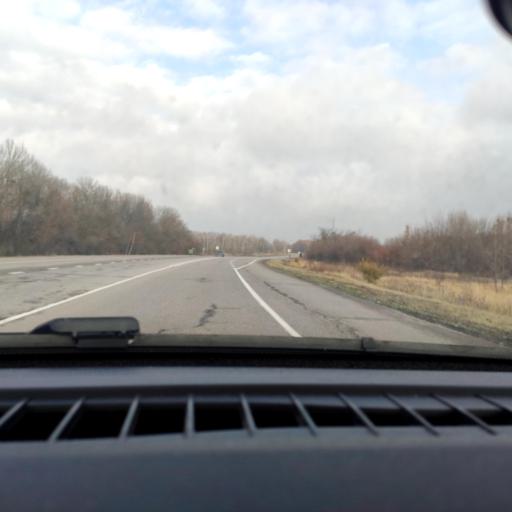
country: RU
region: Voronezj
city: Kolodeznyy
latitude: 51.3161
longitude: 39.0279
